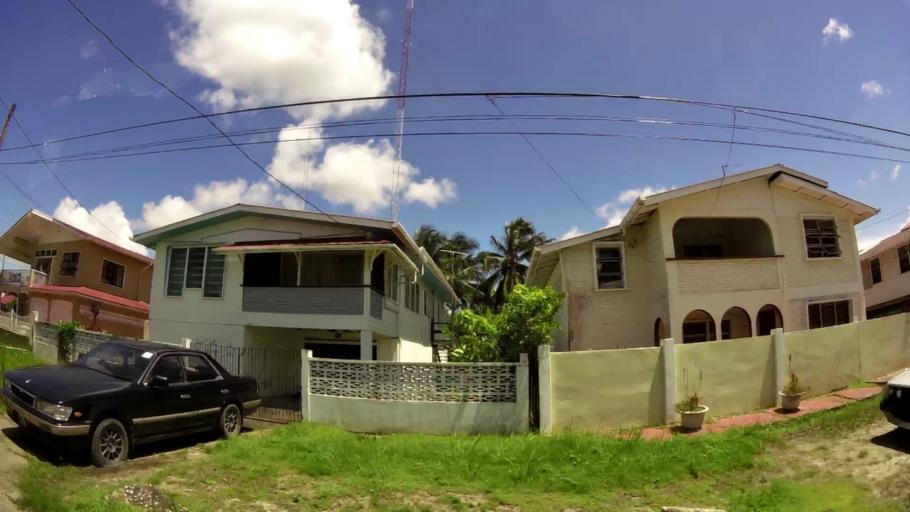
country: GY
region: Demerara-Mahaica
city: Georgetown
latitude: 6.7860
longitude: -58.1483
